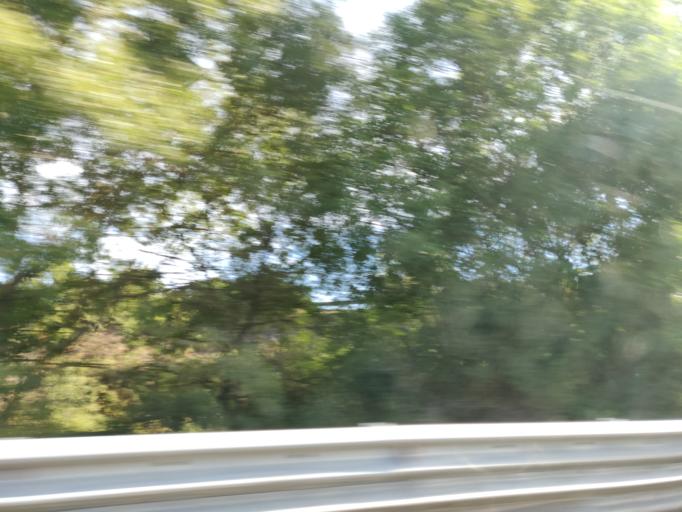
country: IT
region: Tuscany
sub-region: Provincia di Grosseto
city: Ribolla
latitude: 42.9223
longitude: 10.9980
